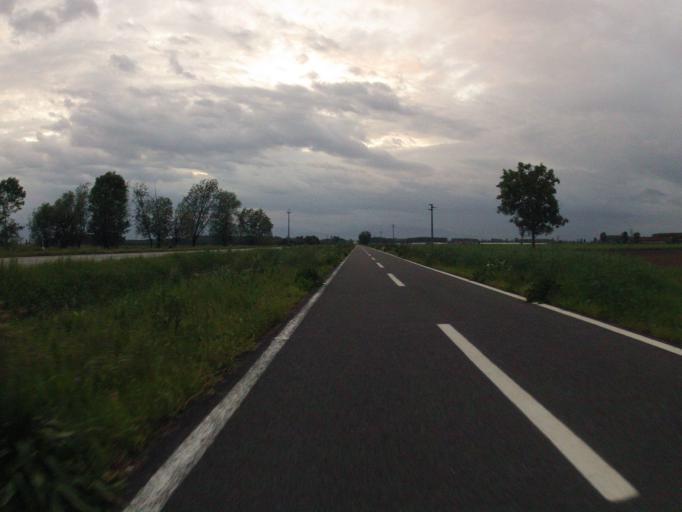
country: IT
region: Piedmont
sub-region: Provincia di Cuneo
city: Moretta
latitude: 44.7712
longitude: 7.5251
